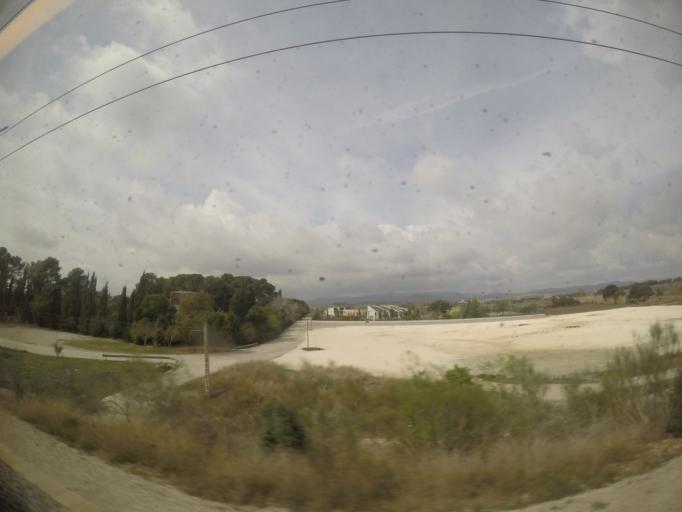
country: ES
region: Catalonia
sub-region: Provincia de Tarragona
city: Santa Oliva
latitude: 41.2642
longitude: 1.5890
